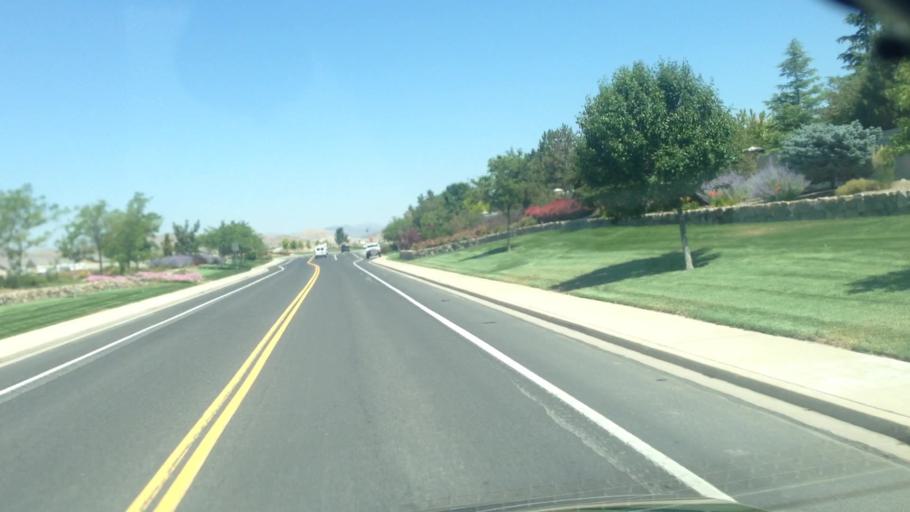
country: US
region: Nevada
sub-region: Washoe County
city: Sparks
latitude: 39.4299
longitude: -119.7164
